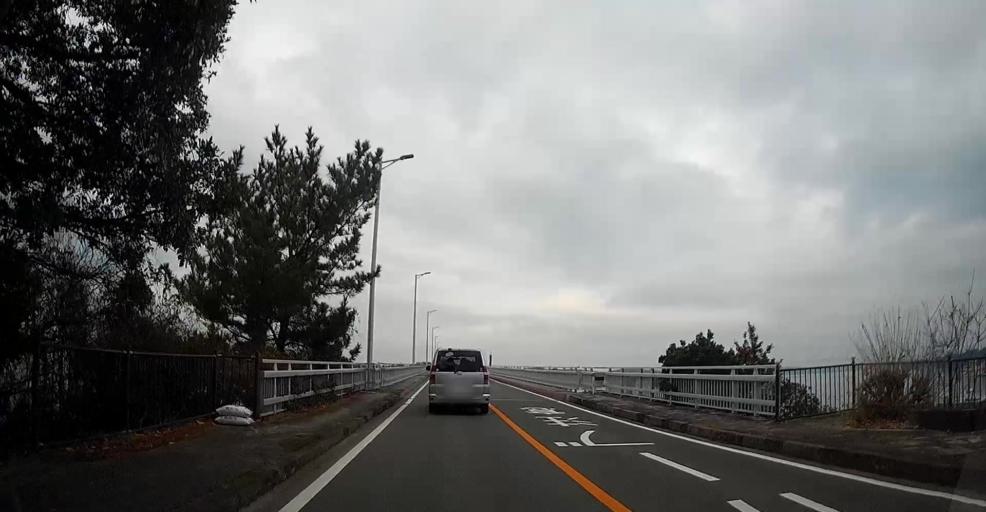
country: JP
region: Kumamoto
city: Yatsushiro
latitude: 32.5272
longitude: 130.4248
